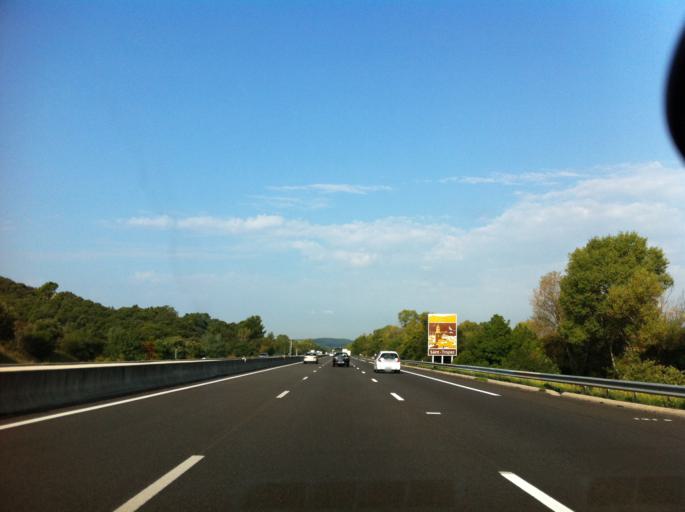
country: FR
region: Provence-Alpes-Cote d'Azur
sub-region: Departement du Var
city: Le Muy
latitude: 43.4596
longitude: 6.5986
